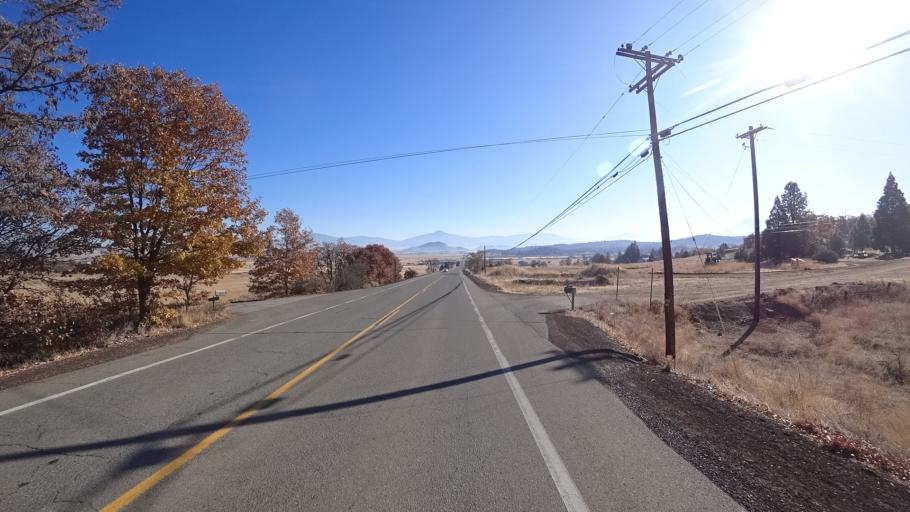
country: US
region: California
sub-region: Siskiyou County
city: Yreka
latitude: 41.7120
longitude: -122.6134
